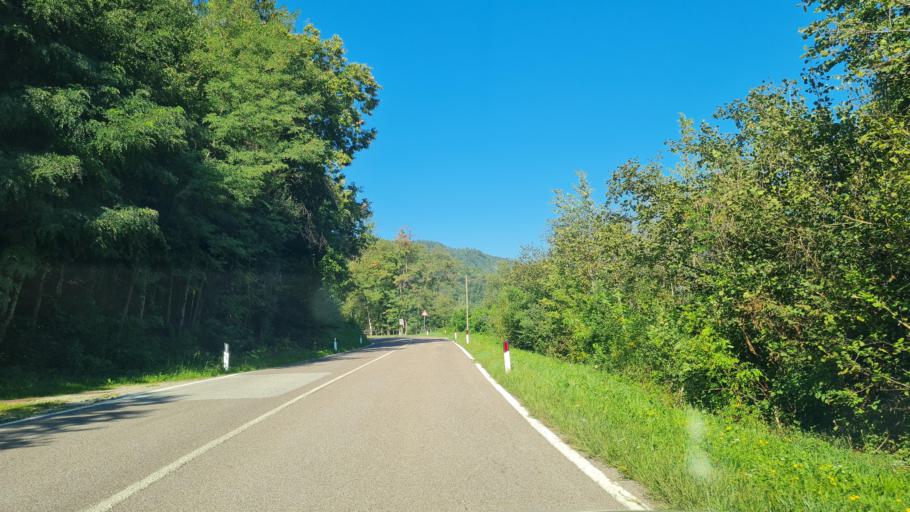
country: IT
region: Trentino-Alto Adige
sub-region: Provincia di Trento
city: Caldonazzo
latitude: 45.9860
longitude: 11.2737
